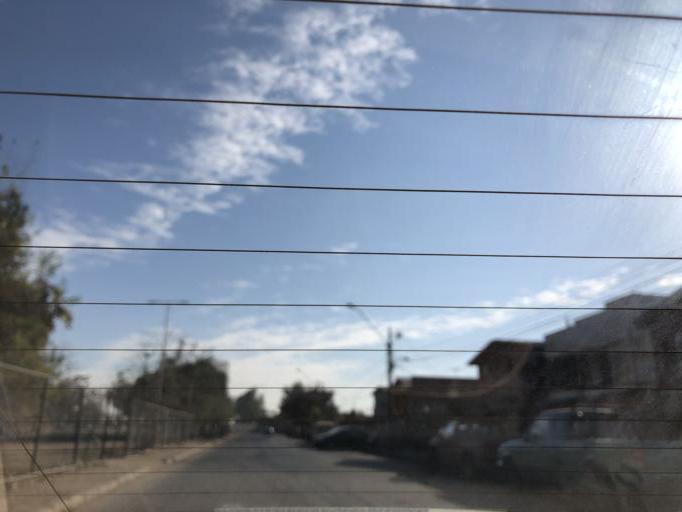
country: CL
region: Santiago Metropolitan
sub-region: Provincia de Cordillera
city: Puente Alto
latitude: -33.6189
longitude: -70.5952
